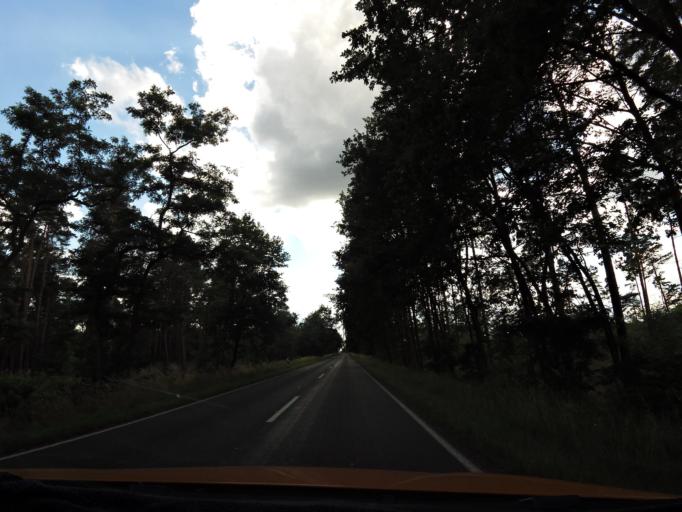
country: DE
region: Brandenburg
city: Wildau
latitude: 52.3099
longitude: 13.7417
